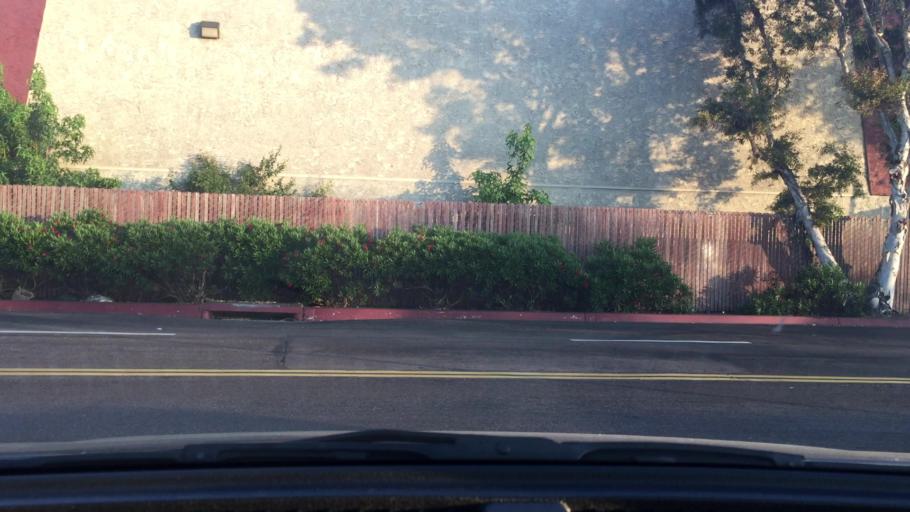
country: US
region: California
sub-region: San Diego County
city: Chula Vista
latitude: 32.6521
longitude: -117.0915
